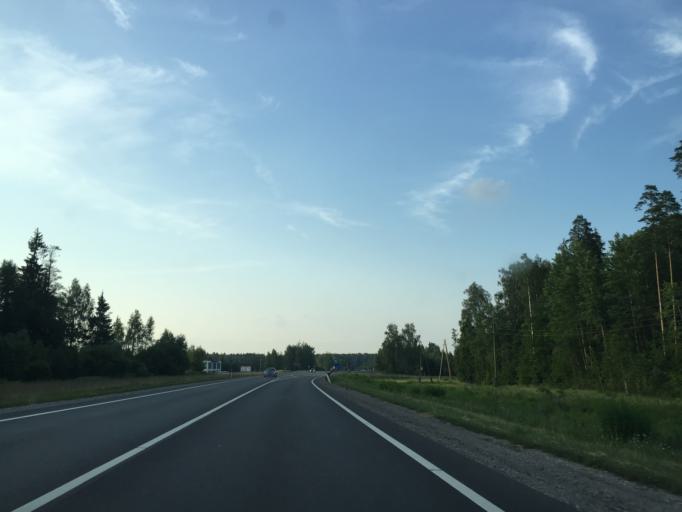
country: LV
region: Ozolnieku
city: Ozolnieki
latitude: 56.6860
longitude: 23.8209
